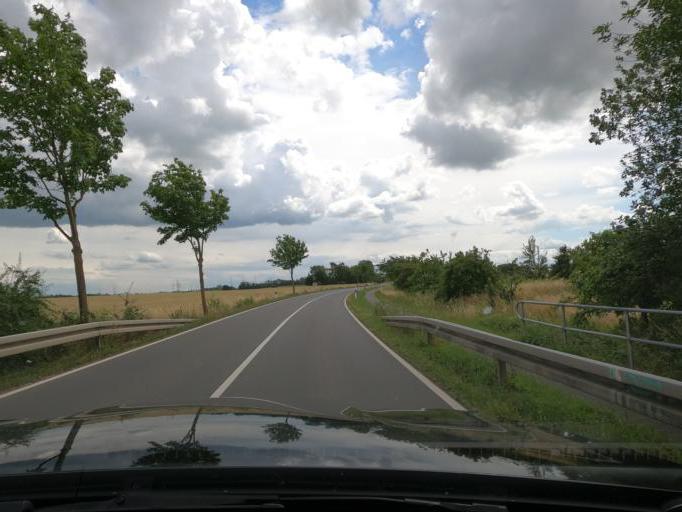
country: DE
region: Lower Saxony
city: Sehnde
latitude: 52.3051
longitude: 9.9777
